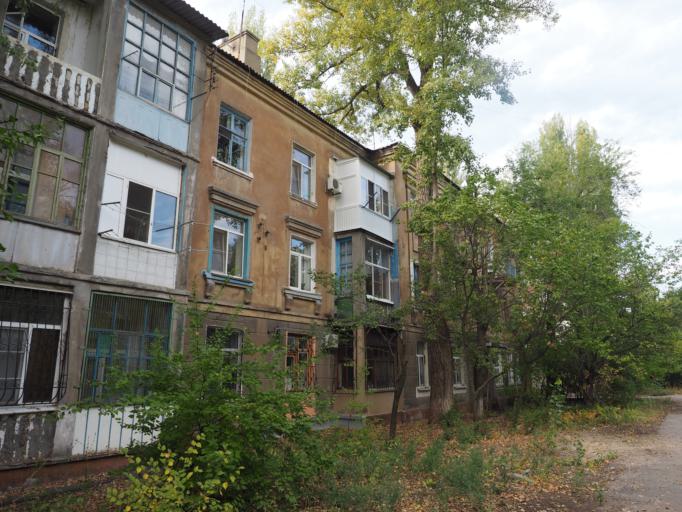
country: RU
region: Volgograd
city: Krasnoslobodsk
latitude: 48.5227
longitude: 44.5103
